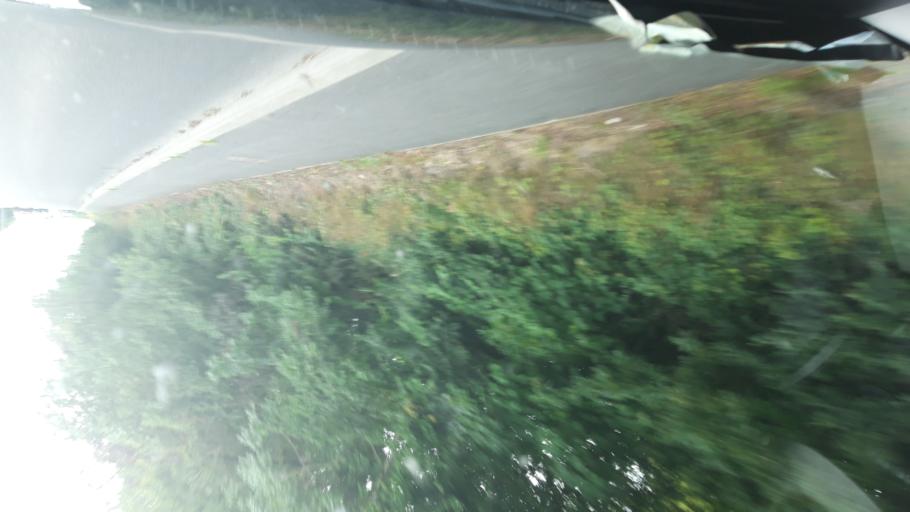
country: IE
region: Leinster
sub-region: Kilkenny
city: Kilkenny
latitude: 52.6376
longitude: -7.2709
